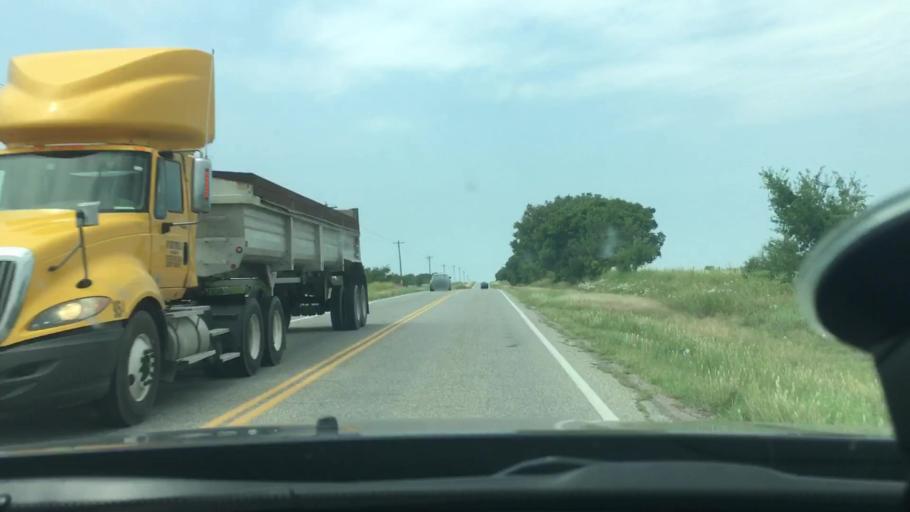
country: US
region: Oklahoma
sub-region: Marshall County
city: Kingston
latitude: 33.9983
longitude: -96.7668
